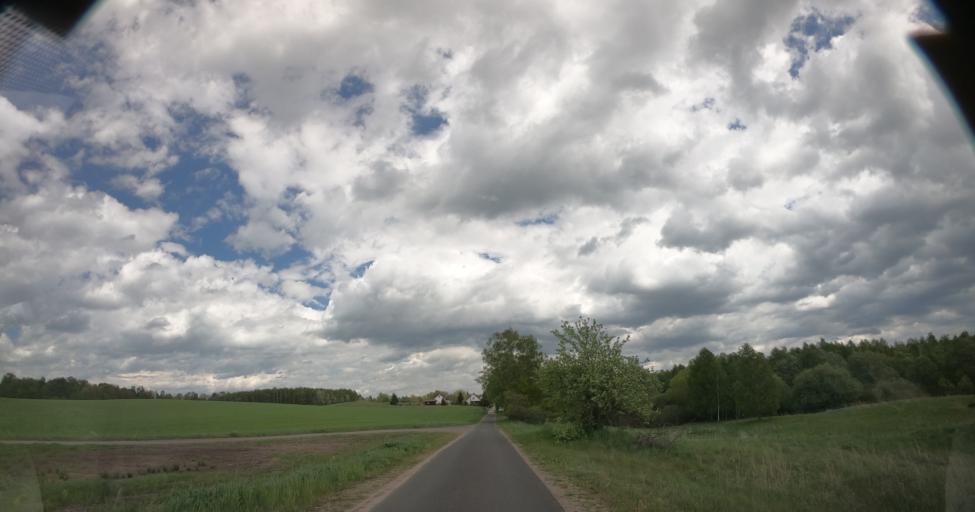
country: PL
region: West Pomeranian Voivodeship
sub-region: Powiat drawski
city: Drawsko Pomorskie
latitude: 53.5629
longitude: 15.7828
